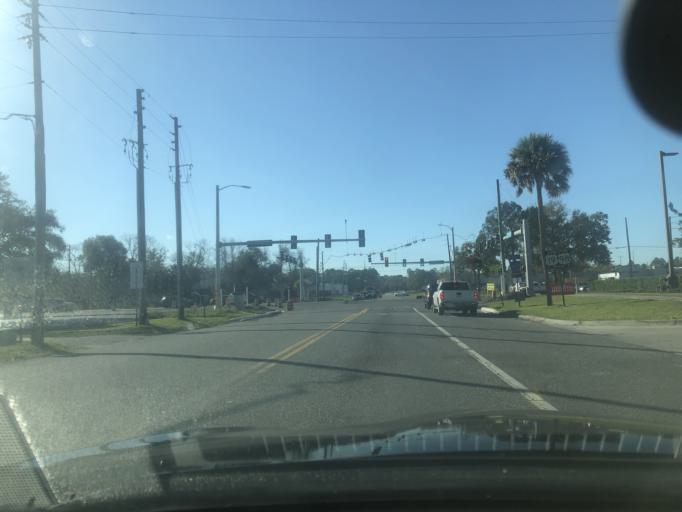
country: US
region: Florida
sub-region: Citrus County
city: Homosassa Springs
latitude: 28.8056
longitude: -82.5756
